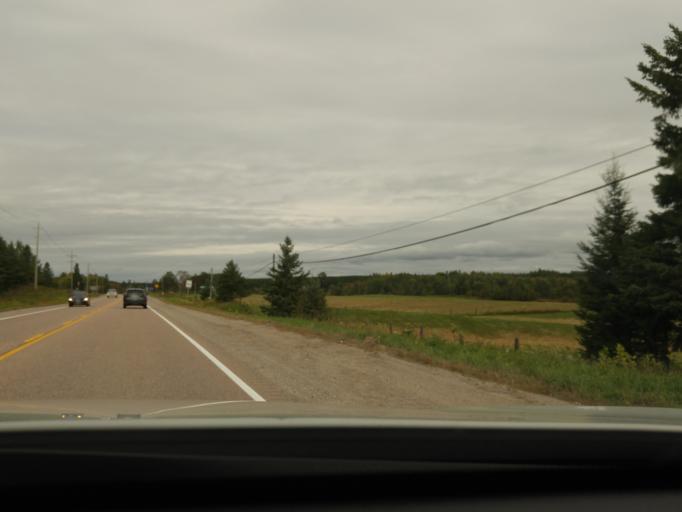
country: CA
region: Ontario
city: Renfrew
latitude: 45.5823
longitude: -76.8257
